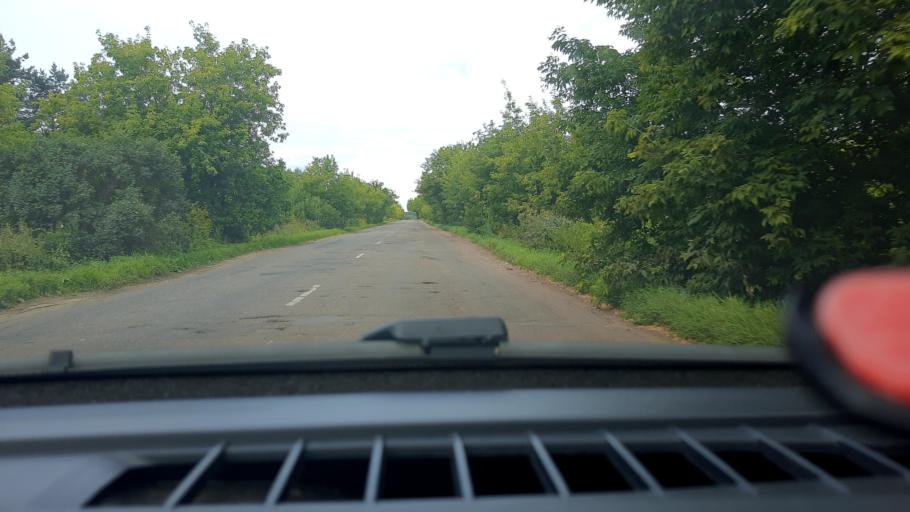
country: RU
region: Nizjnij Novgorod
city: Bogorodsk
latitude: 56.0667
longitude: 43.5901
